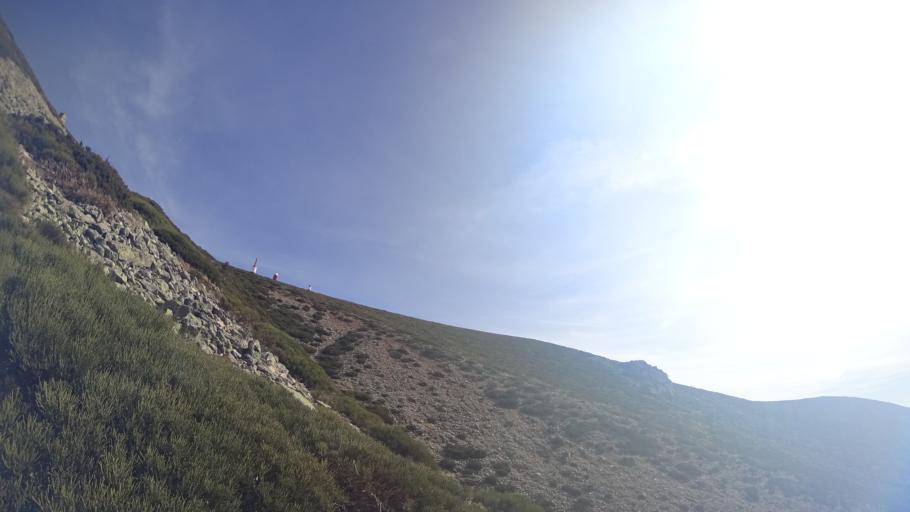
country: ES
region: Madrid
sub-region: Provincia de Madrid
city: Navacerrada
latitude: 40.7843
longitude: -3.9857
